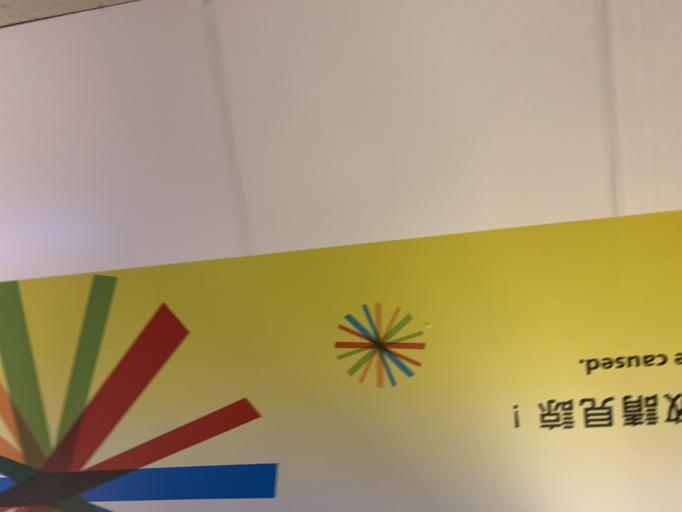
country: TW
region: Taiwan
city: Taoyuan City
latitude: 25.0785
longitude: 121.2362
